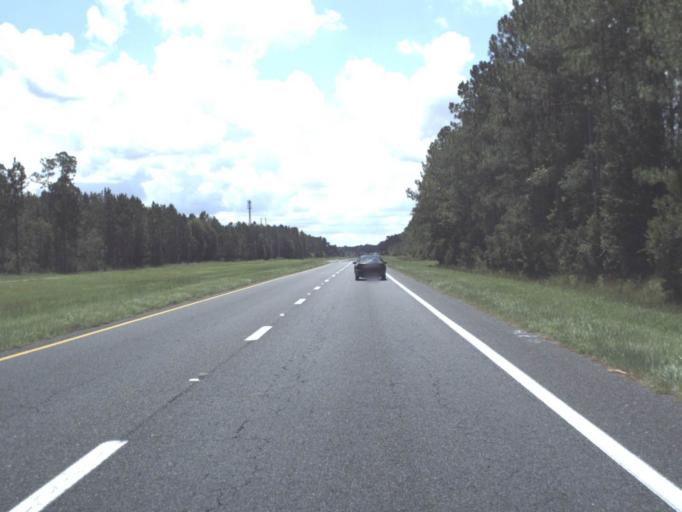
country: US
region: Florida
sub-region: Levy County
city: Bronson
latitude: 29.4596
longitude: -82.6594
